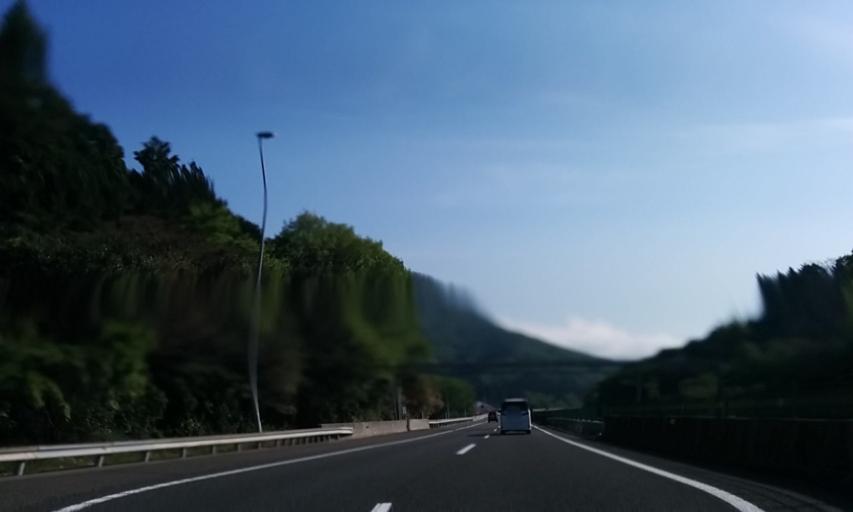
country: JP
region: Gifu
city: Tarui
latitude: 35.3420
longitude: 136.4078
